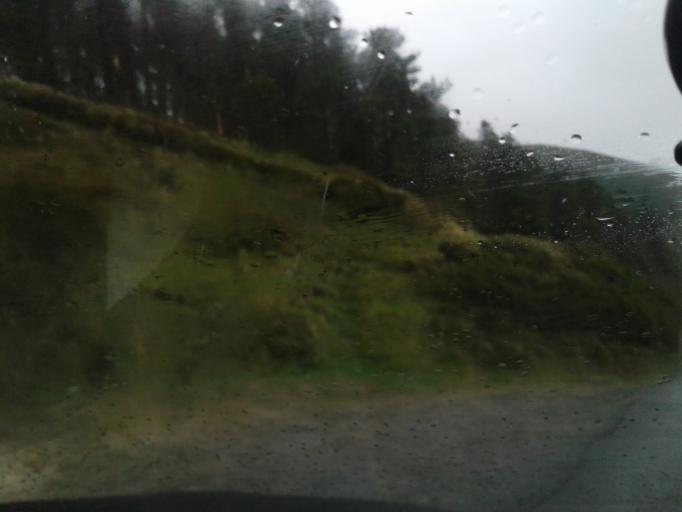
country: IE
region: Leinster
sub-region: Wicklow
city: Enniskerry
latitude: 53.1127
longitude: -6.2606
